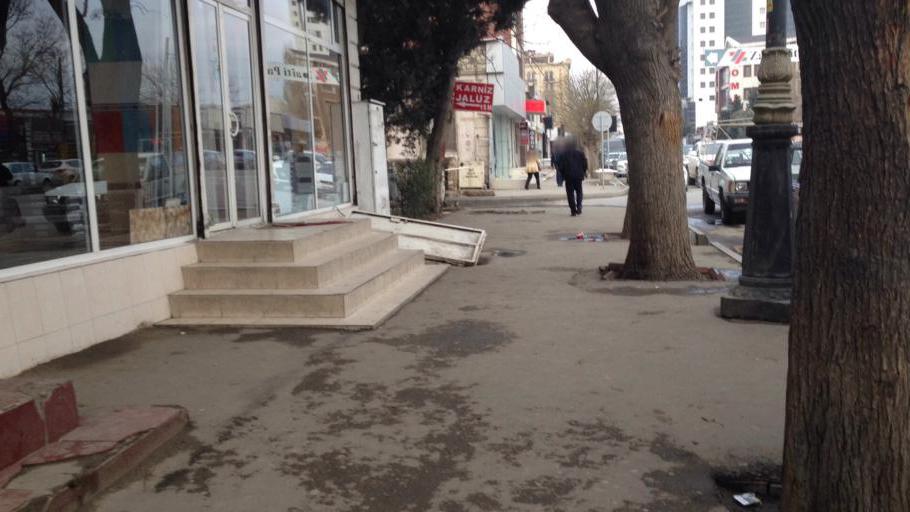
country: AZ
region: Baki
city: Baku
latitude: 40.3883
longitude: 49.8580
